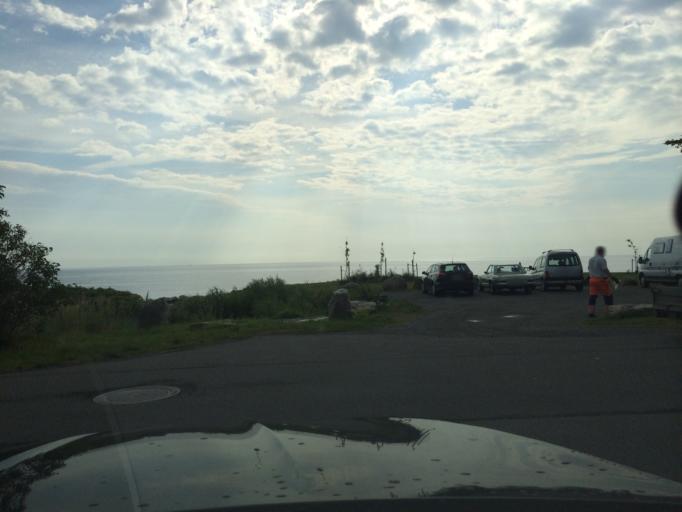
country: SE
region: Skane
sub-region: Simrishamns Kommun
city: Simrishamn
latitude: 55.5155
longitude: 14.3476
